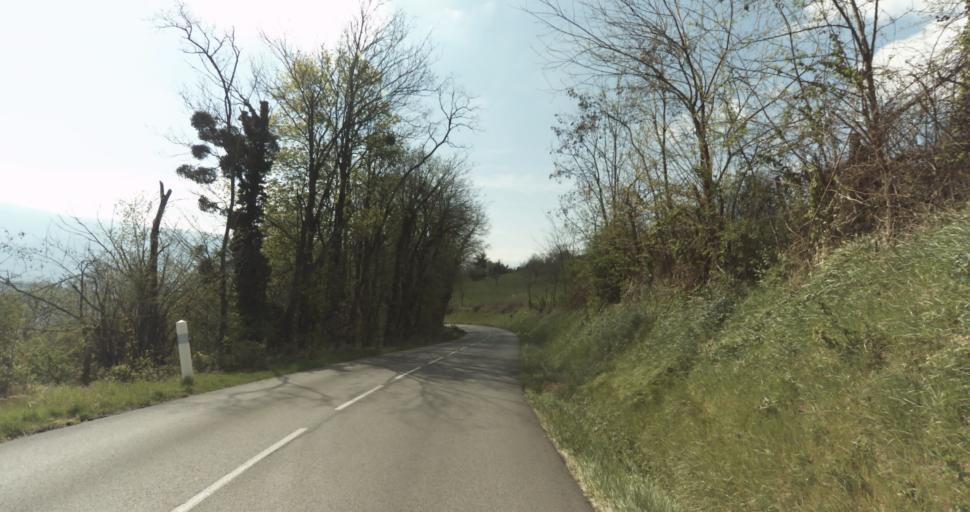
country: FR
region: Rhone-Alpes
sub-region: Departement de l'Isere
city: Saint-Verand
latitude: 45.1701
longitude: 5.3215
